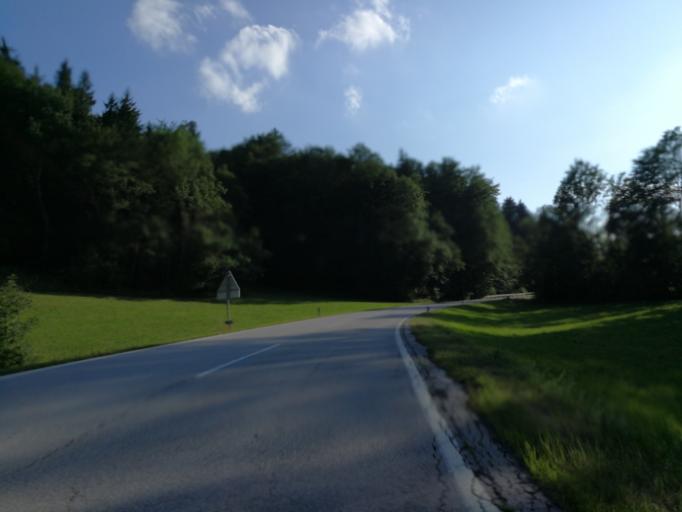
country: AT
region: Salzburg
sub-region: Politischer Bezirk Salzburg-Umgebung
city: Plainfeld
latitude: 47.8317
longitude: 13.1634
